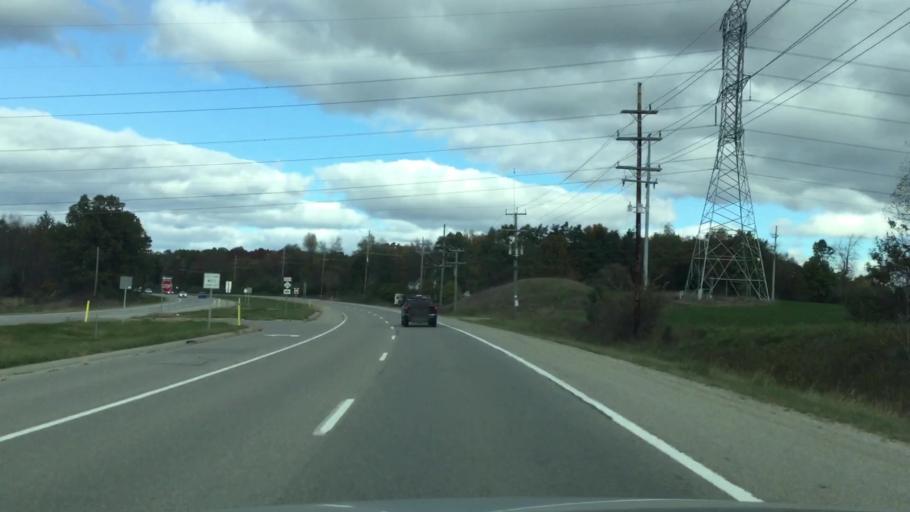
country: US
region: Michigan
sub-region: Lapeer County
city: Lapeer
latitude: 42.9876
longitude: -83.3152
